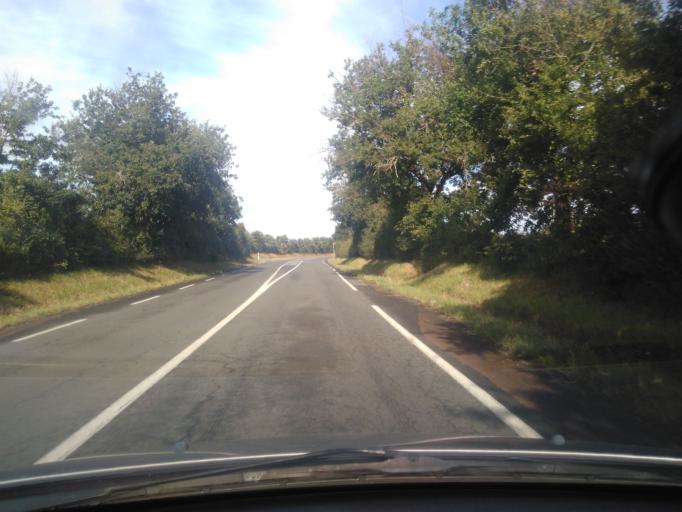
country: FR
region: Pays de la Loire
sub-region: Departement de la Vendee
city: Chateau-d'Olonne
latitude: 46.5264
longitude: -1.7433
